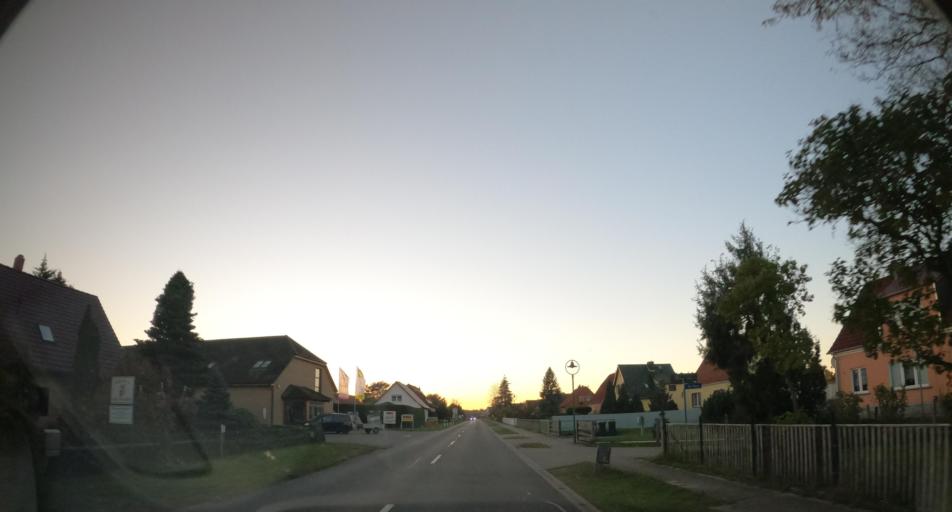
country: DE
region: Mecklenburg-Vorpommern
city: Ueckermunde
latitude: 53.7670
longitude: 13.9704
